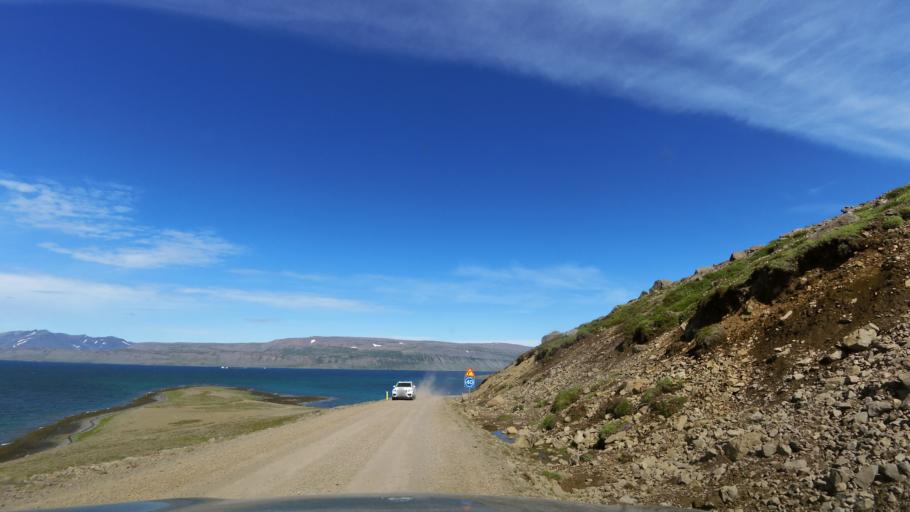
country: IS
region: Westfjords
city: Isafjoerdur
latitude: 65.6304
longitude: -23.5025
